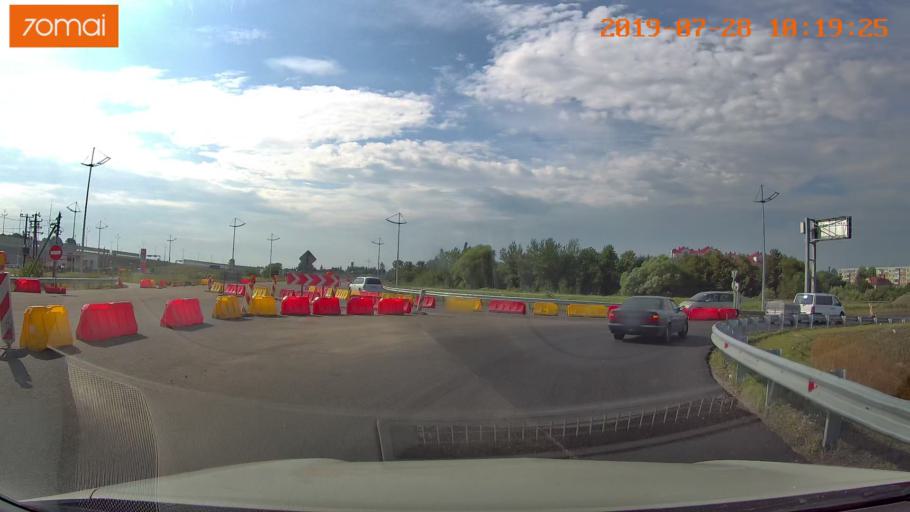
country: RU
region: Kaliningrad
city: Maloye Isakovo
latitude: 54.7483
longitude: 20.5866
